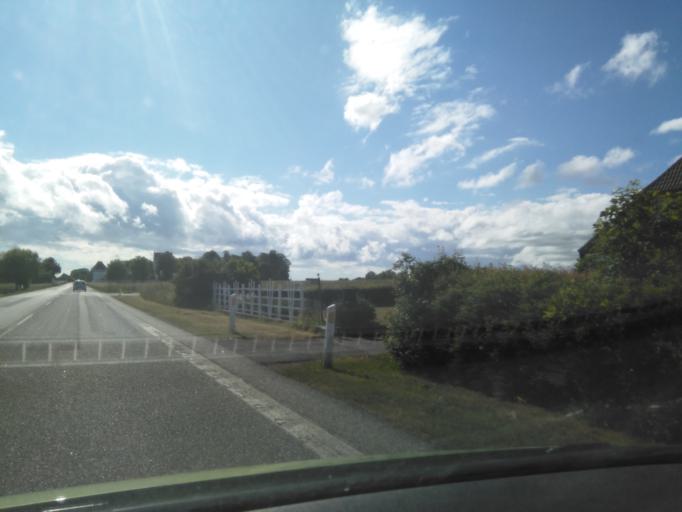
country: DK
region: Capital Region
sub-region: Bornholm Kommune
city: Nexo
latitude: 55.0624
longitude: 15.0779
